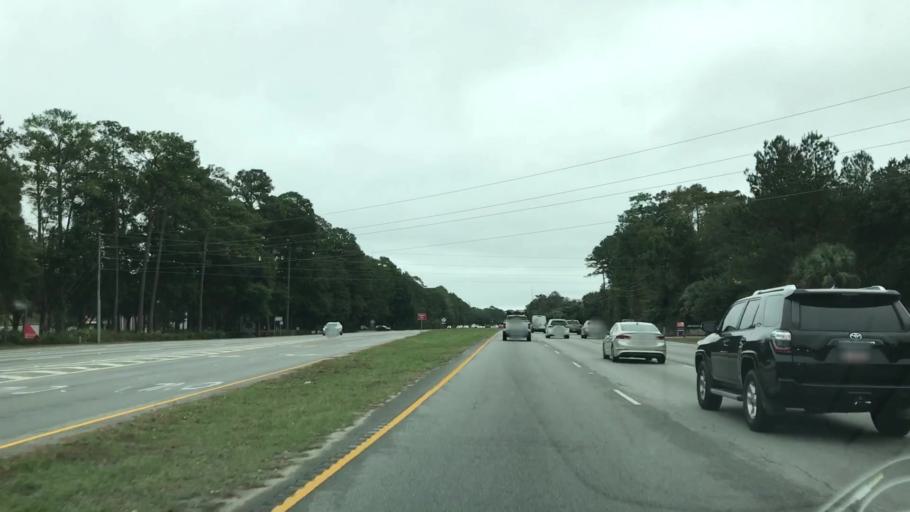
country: US
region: South Carolina
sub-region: Beaufort County
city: Bluffton
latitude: 32.2677
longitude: -80.8607
